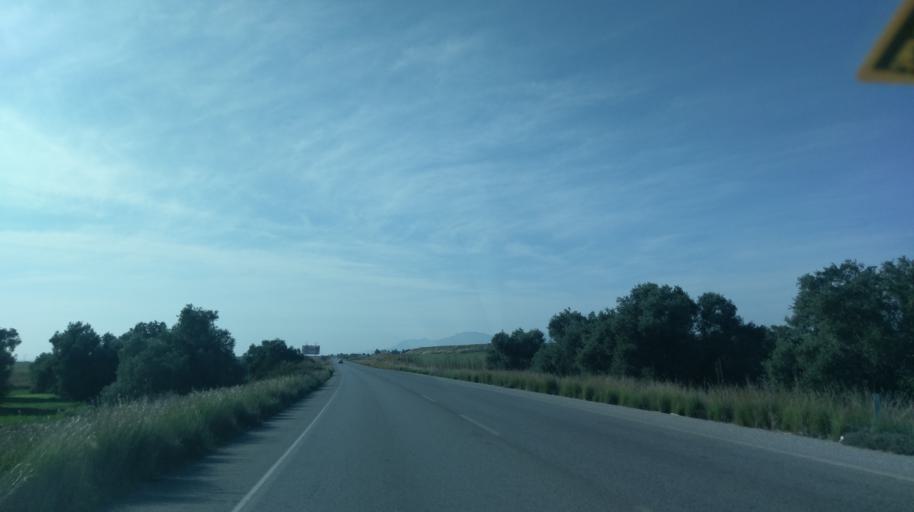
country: CY
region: Ammochostos
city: Lefkonoiko
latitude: 35.2614
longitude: 33.7751
